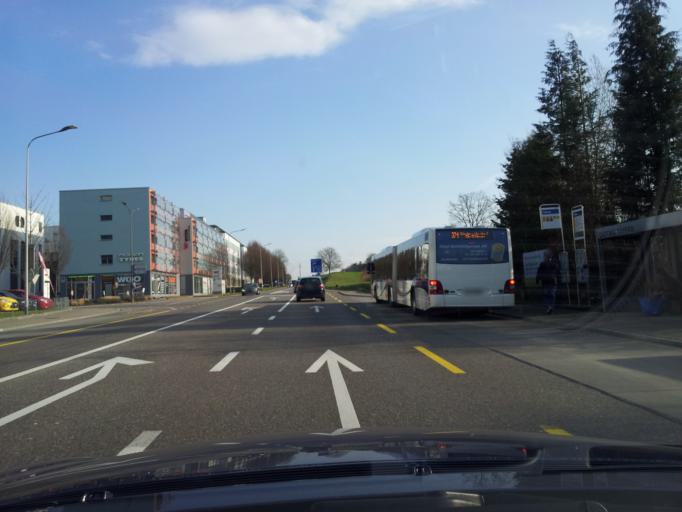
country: CH
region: Aargau
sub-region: Bezirk Baden
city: Baden
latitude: 47.4495
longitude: 8.2914
